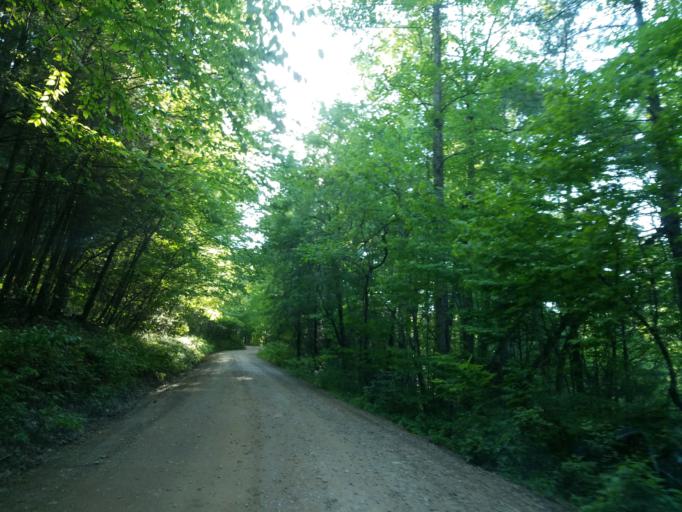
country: US
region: Georgia
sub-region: Fannin County
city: Blue Ridge
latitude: 34.7178
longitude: -84.1521
